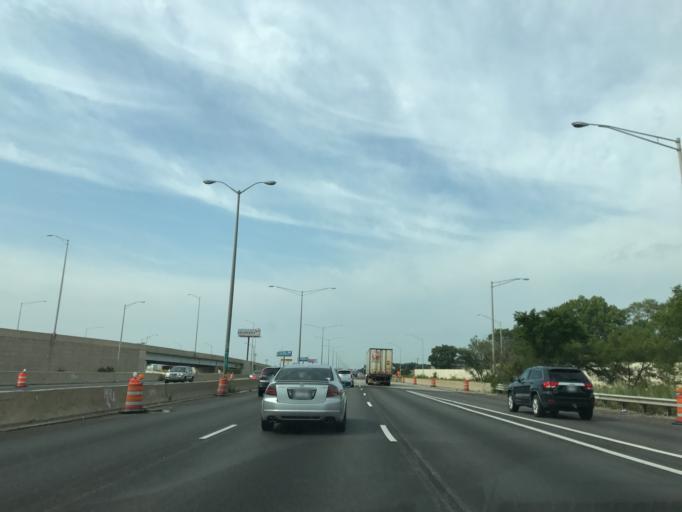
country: US
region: Illinois
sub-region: Will County
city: Bolingbrook
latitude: 41.7003
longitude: -88.0389
